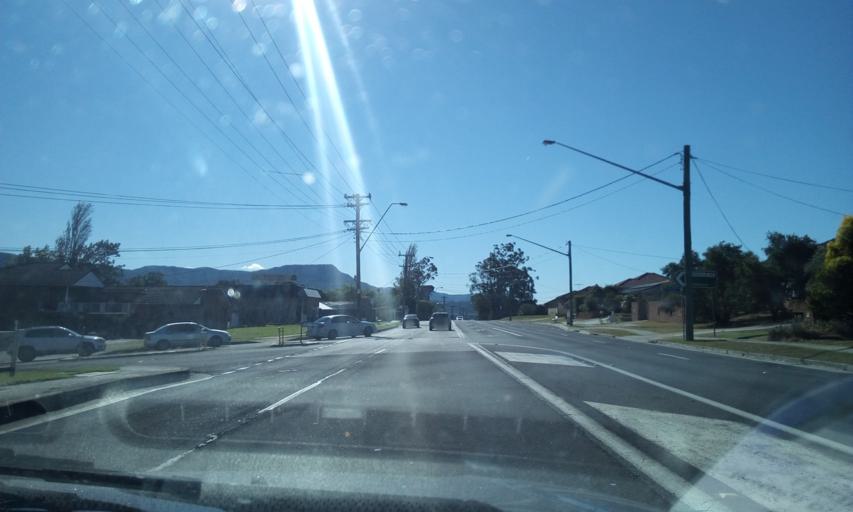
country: AU
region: New South Wales
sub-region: Wollongong
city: Dapto
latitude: -34.5056
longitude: 150.7867
